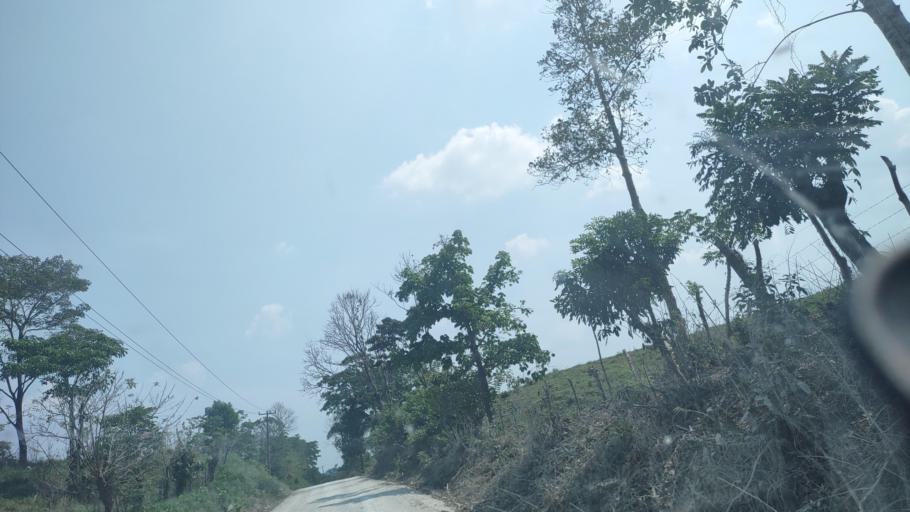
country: MX
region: Tabasco
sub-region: Huimanguillo
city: Francisco Rueda
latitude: 17.5864
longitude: -93.8920
